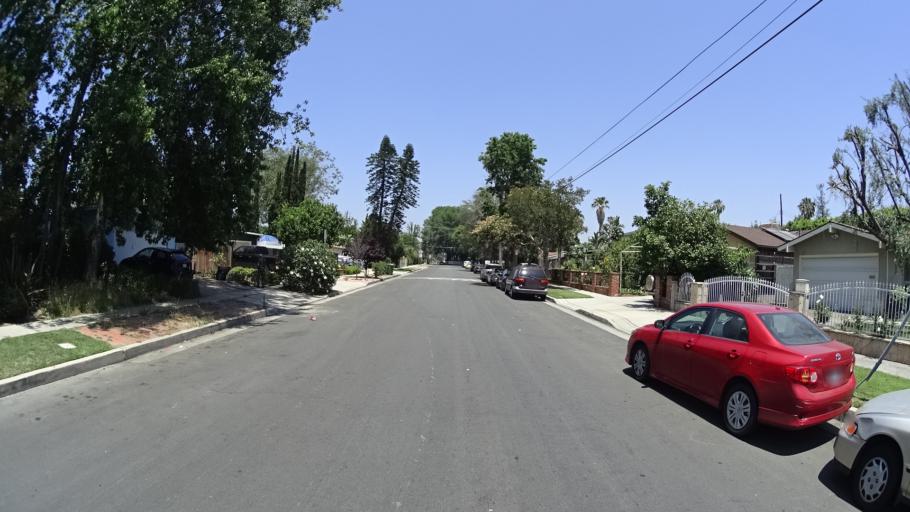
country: US
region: California
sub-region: Los Angeles County
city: Van Nuys
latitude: 34.1962
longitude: -118.4324
